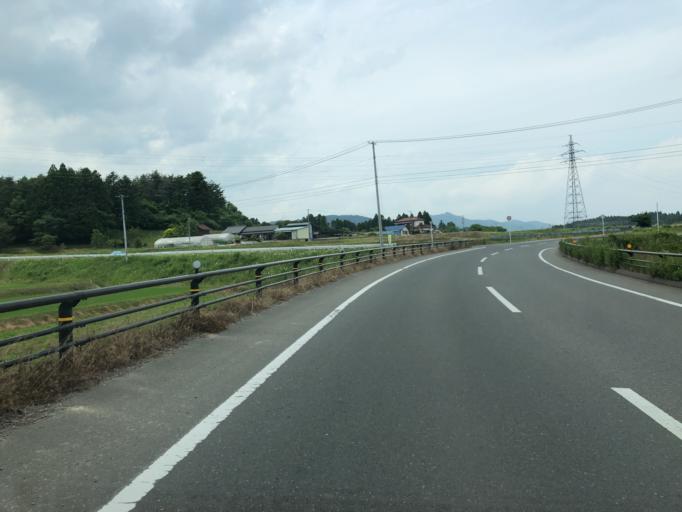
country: JP
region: Miyagi
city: Marumori
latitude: 37.8102
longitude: 140.8941
